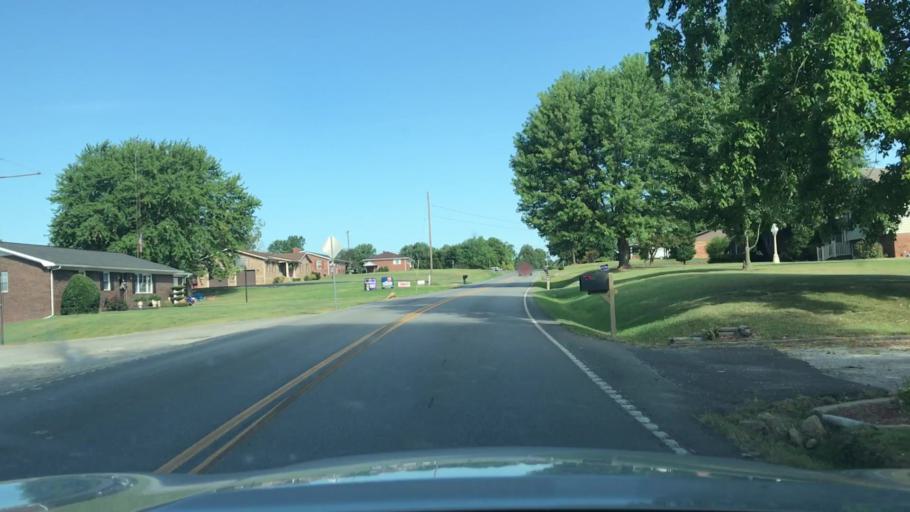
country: US
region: Kentucky
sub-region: Muhlenberg County
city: Greenville
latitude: 37.1873
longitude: -87.1663
